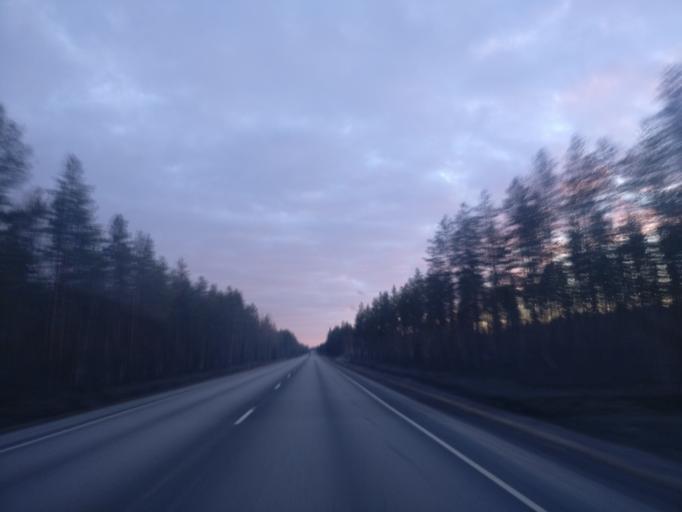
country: FI
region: Northern Ostrobothnia
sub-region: Nivala-Haapajaervi
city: Kaersaemaeki
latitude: 64.0955
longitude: 25.8011
